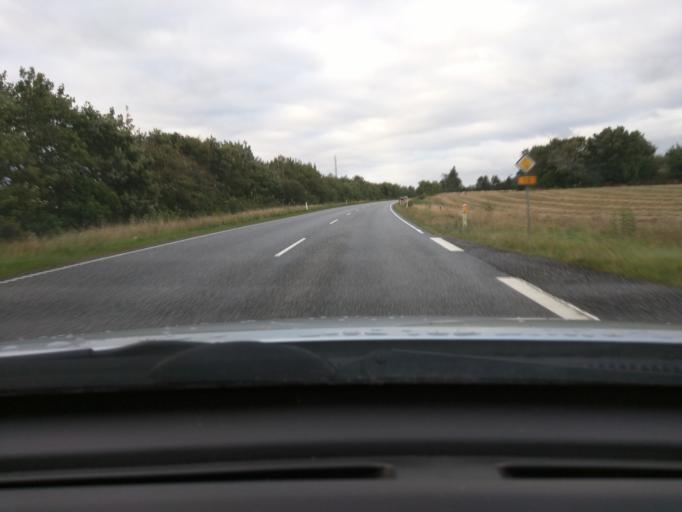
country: DK
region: Central Jutland
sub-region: Ikast-Brande Kommune
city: Bording Kirkeby
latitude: 56.2359
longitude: 9.3235
